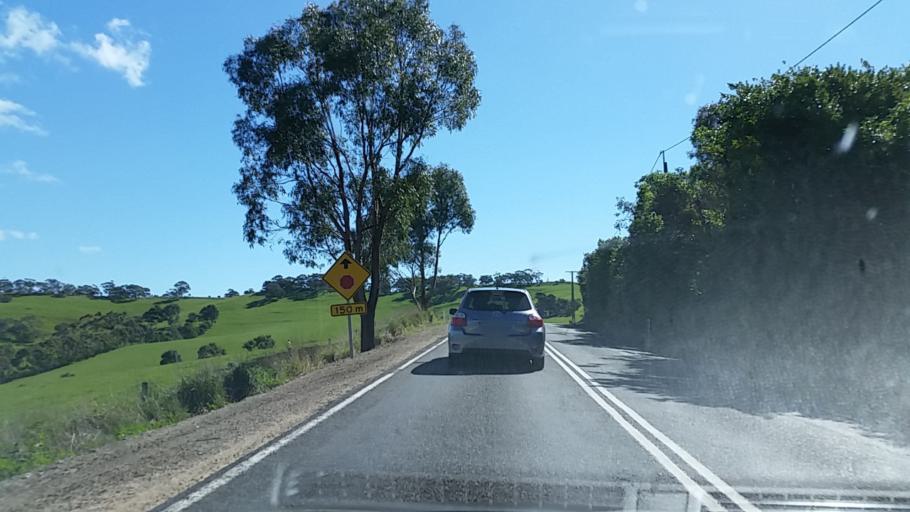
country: AU
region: South Australia
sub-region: Mount Barker
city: Meadows
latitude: -35.1979
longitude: 138.7734
